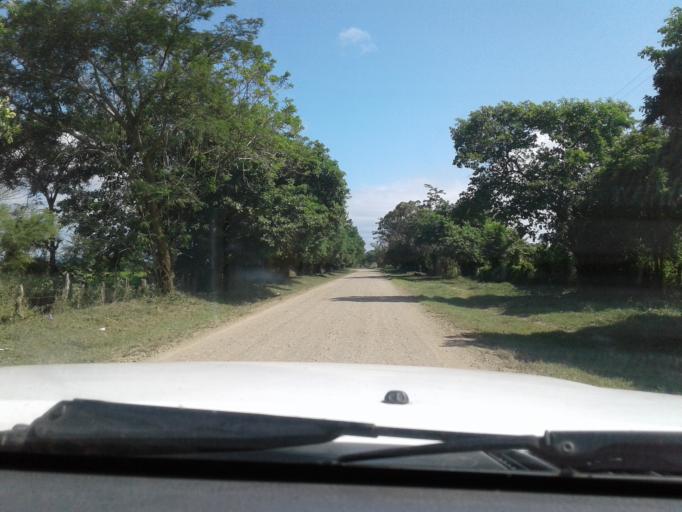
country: NI
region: Rivas
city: Belen
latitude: 11.6259
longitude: -85.9436
